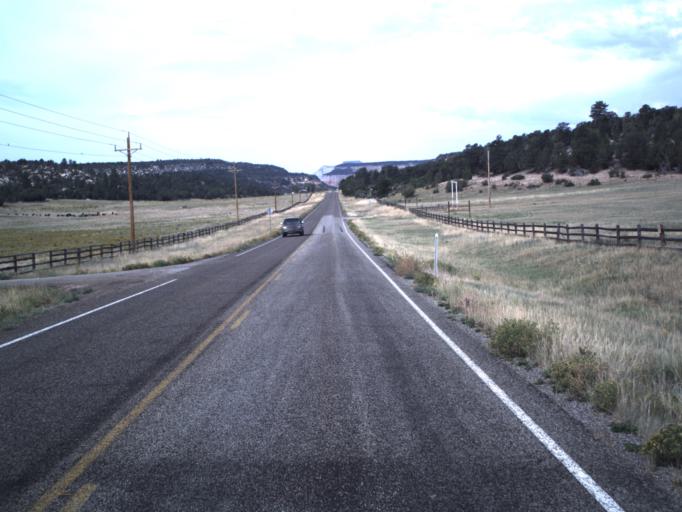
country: US
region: Utah
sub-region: Washington County
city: Hildale
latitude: 37.2425
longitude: -112.8131
